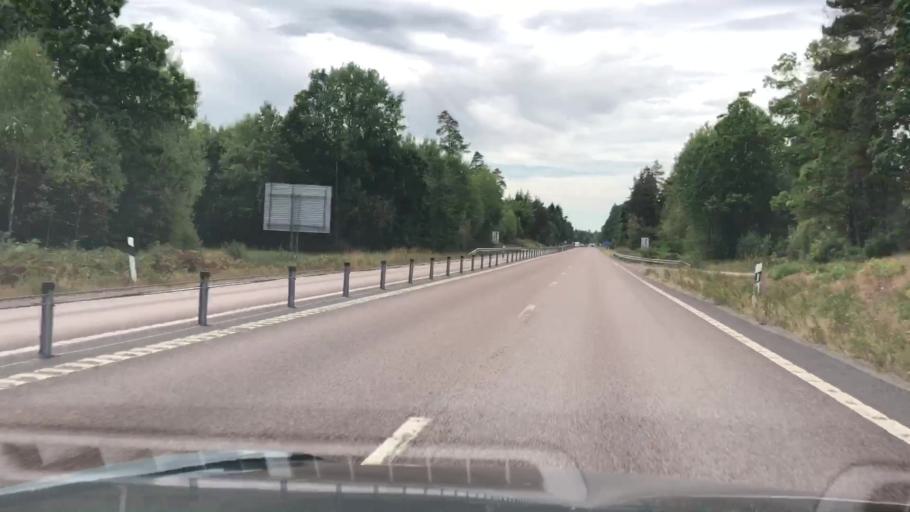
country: SE
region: Kalmar
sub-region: Torsas Kommun
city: Torsas
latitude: 56.2865
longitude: 15.9841
